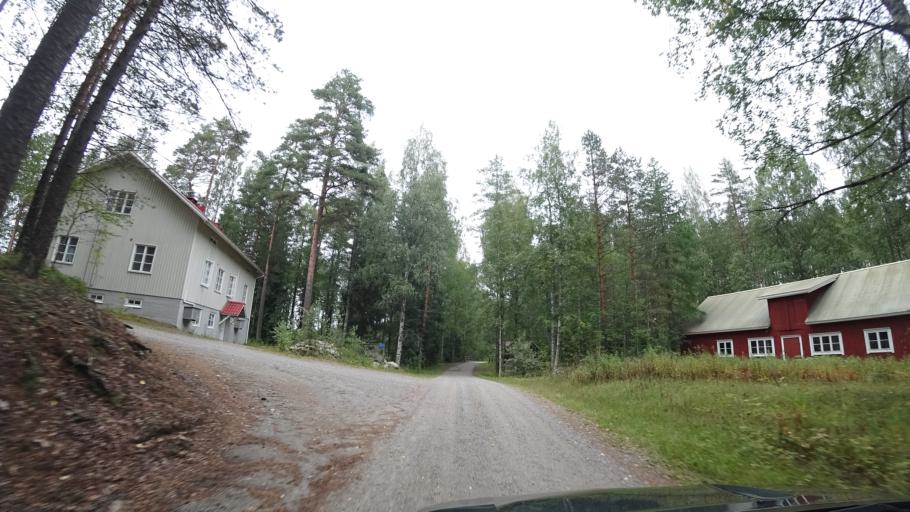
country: FI
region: Paijanne Tavastia
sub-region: Lahti
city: Auttoinen
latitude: 61.2209
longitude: 25.1427
